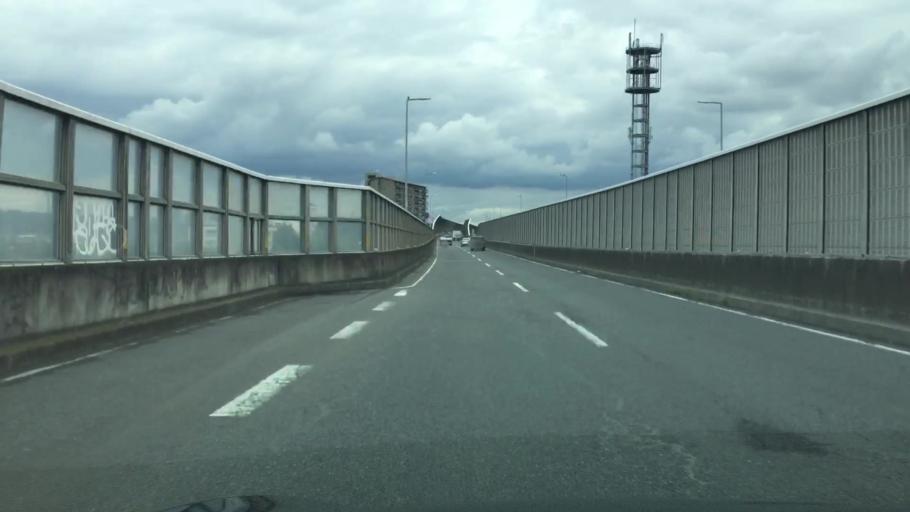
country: JP
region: Saitama
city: Kamifukuoka
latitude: 35.9201
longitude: 139.5599
